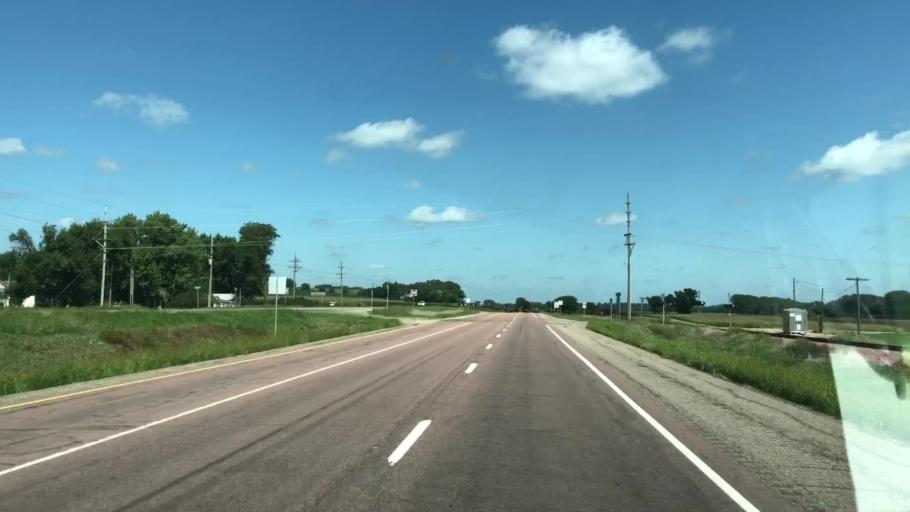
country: US
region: Iowa
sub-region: Woodbury County
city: Sioux City
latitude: 42.5761
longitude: -96.3165
